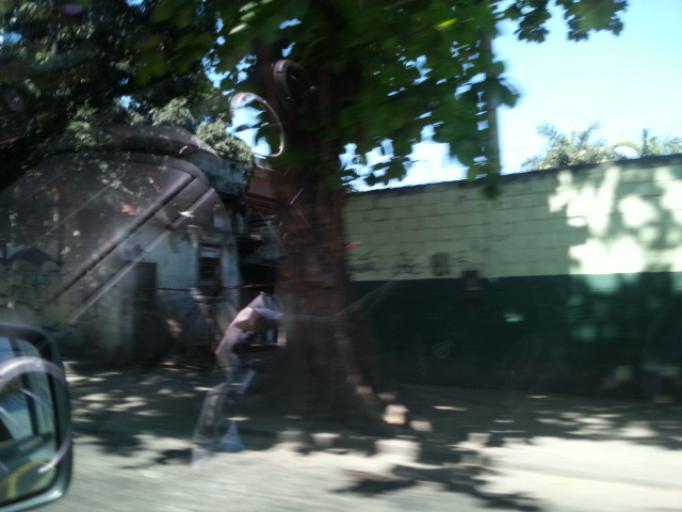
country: BR
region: Rio de Janeiro
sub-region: Rio De Janeiro
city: Rio de Janeiro
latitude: -22.8959
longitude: -43.2153
